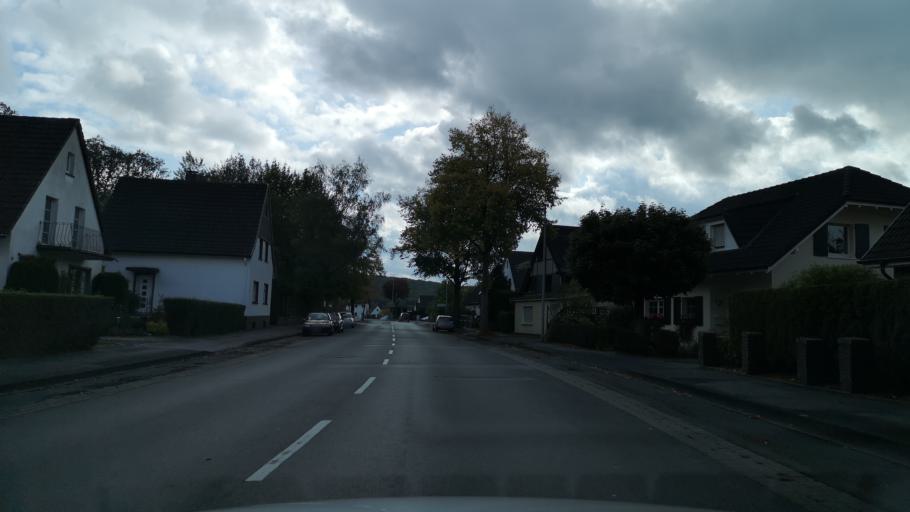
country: DE
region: North Rhine-Westphalia
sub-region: Regierungsbezirk Arnsberg
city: Menden
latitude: 51.4396
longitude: 7.7647
